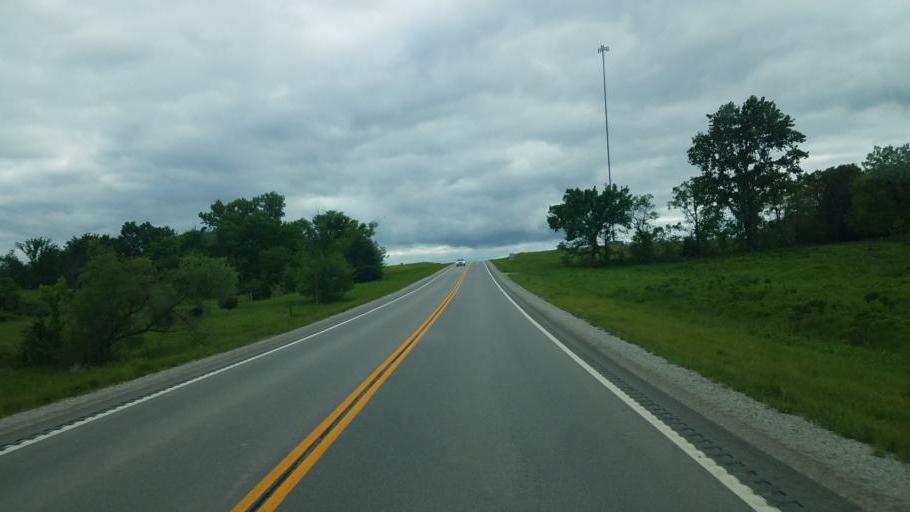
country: US
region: Missouri
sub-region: Harrison County
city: Bethany
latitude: 40.3214
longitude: -93.8010
